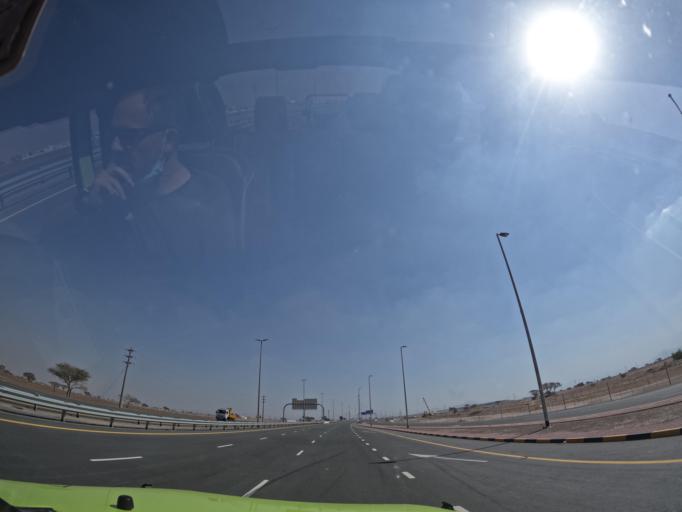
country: AE
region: Ash Shariqah
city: Adh Dhayd
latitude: 24.9115
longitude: 55.7894
